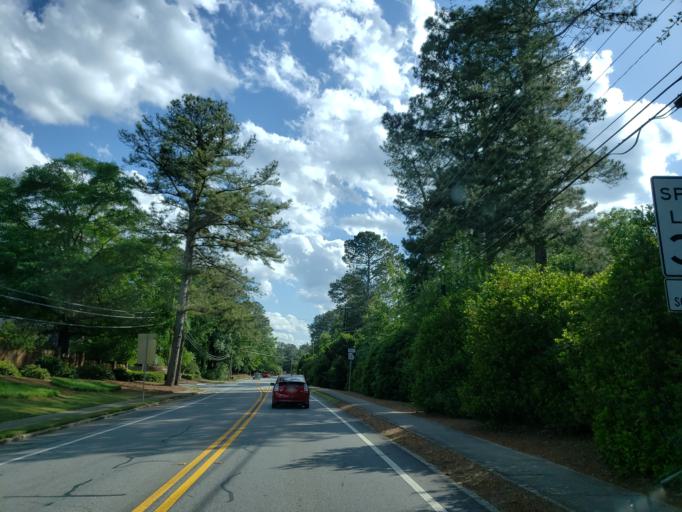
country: US
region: Georgia
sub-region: DeKalb County
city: Clarkston
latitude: 33.8365
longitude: -84.2705
